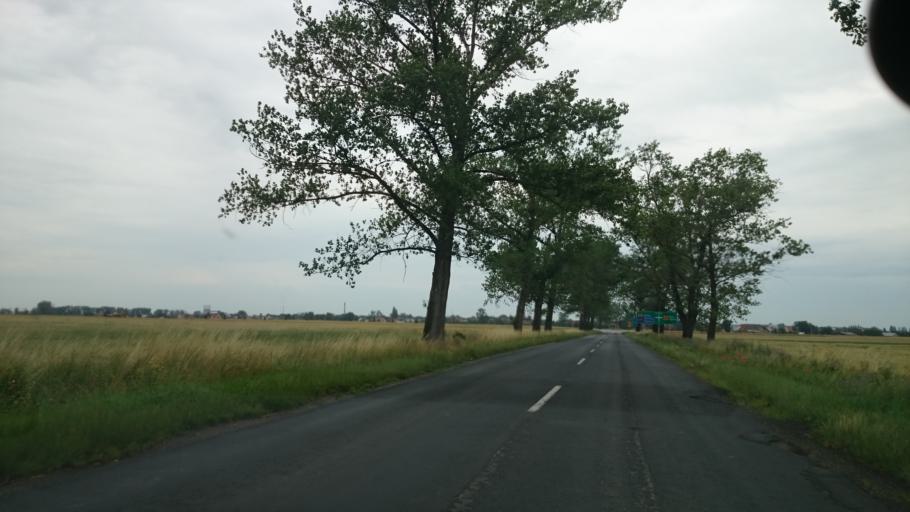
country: PL
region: Opole Voivodeship
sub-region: Powiat brzeski
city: Grodkow
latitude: 50.6878
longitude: 17.3601
